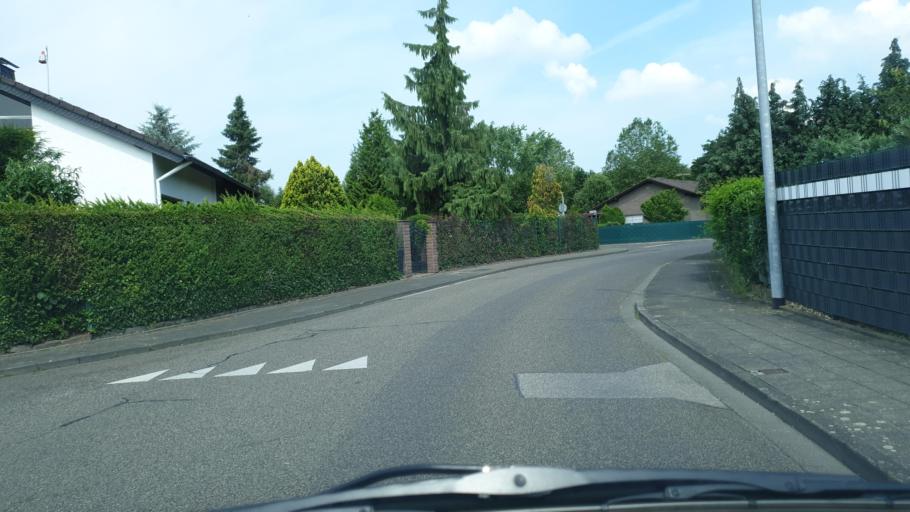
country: DE
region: North Rhine-Westphalia
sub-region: Regierungsbezirk Koln
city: Bergheim
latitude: 50.9383
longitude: 6.6688
